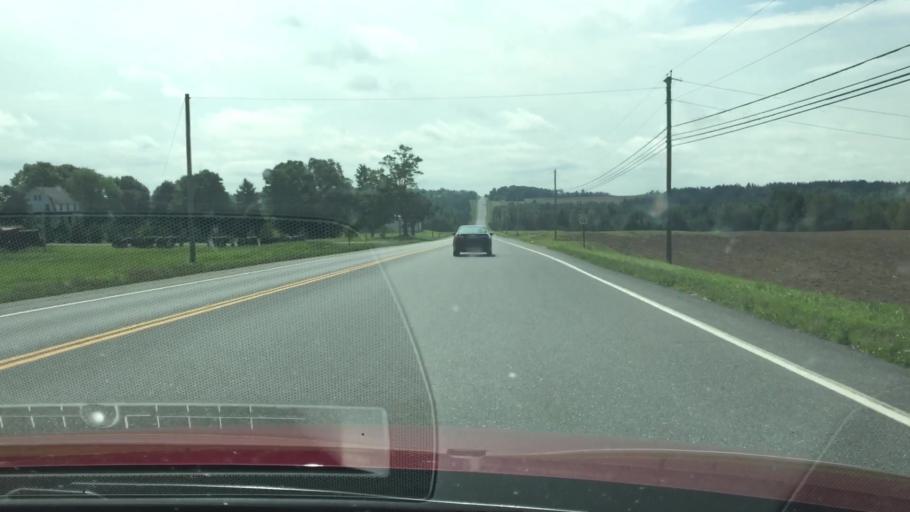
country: CA
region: New Brunswick
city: Florenceville-Bristol
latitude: 46.4111
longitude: -67.8433
